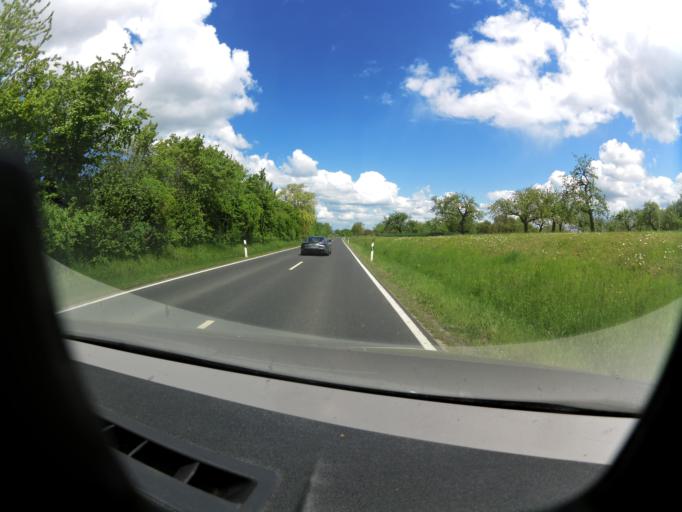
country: DE
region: Bavaria
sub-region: Regierungsbezirk Unterfranken
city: Waigolshausen
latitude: 49.9559
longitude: 10.1465
